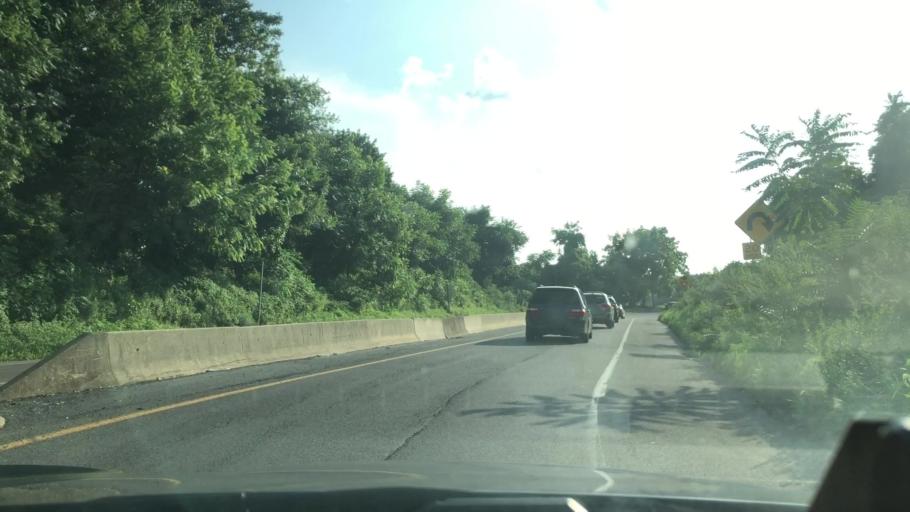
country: US
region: Pennsylvania
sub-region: Lehigh County
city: Allentown
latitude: 40.6176
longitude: -75.5006
